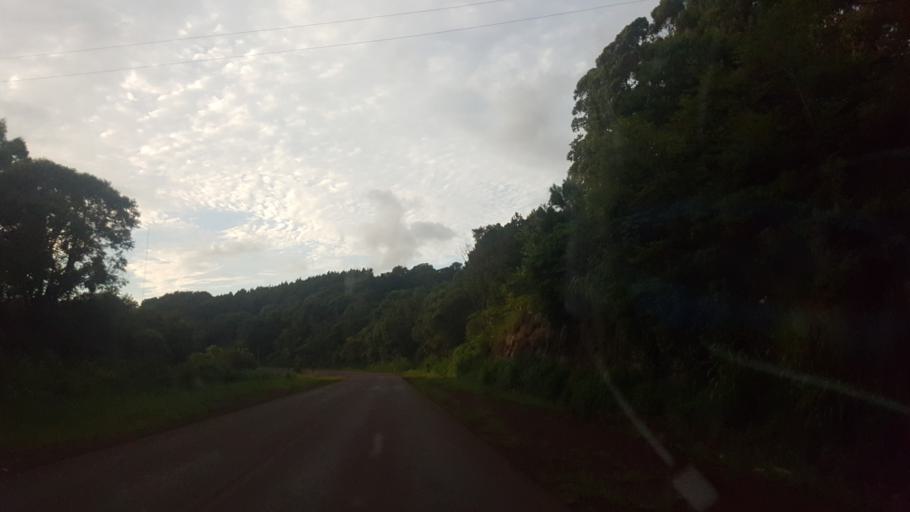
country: AR
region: Misiones
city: Dos de Mayo
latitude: -27.0106
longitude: -54.6909
